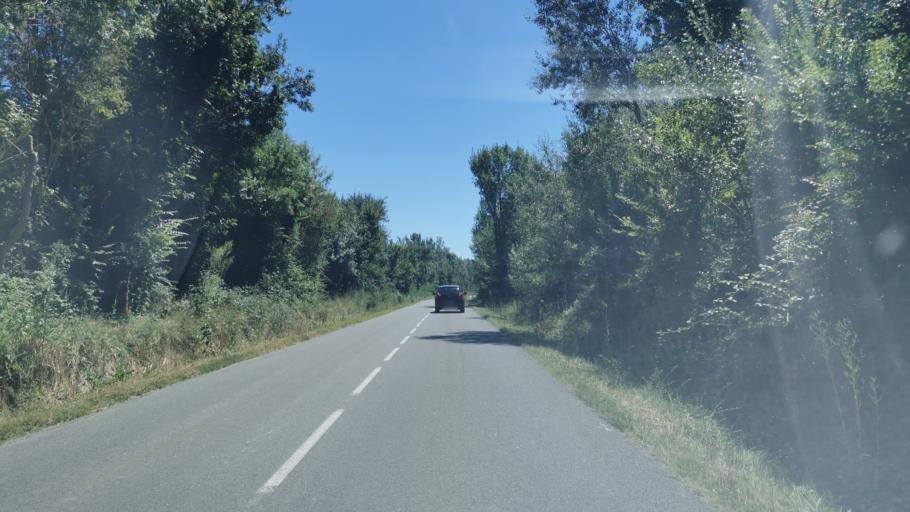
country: FR
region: Languedoc-Roussillon
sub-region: Departement de l'Aude
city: Vinassan
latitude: 43.2243
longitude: 3.0772
